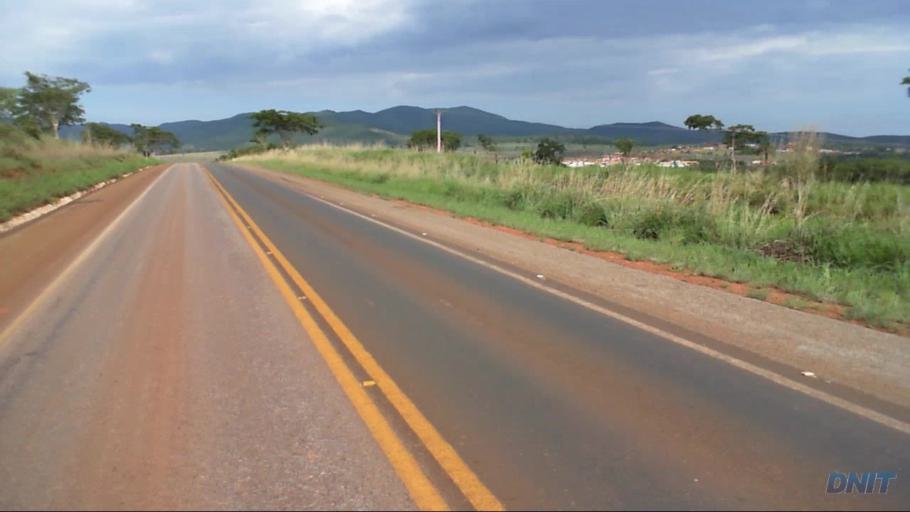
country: BR
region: Goias
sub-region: Barro Alto
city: Barro Alto
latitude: -14.9877
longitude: -48.9136
